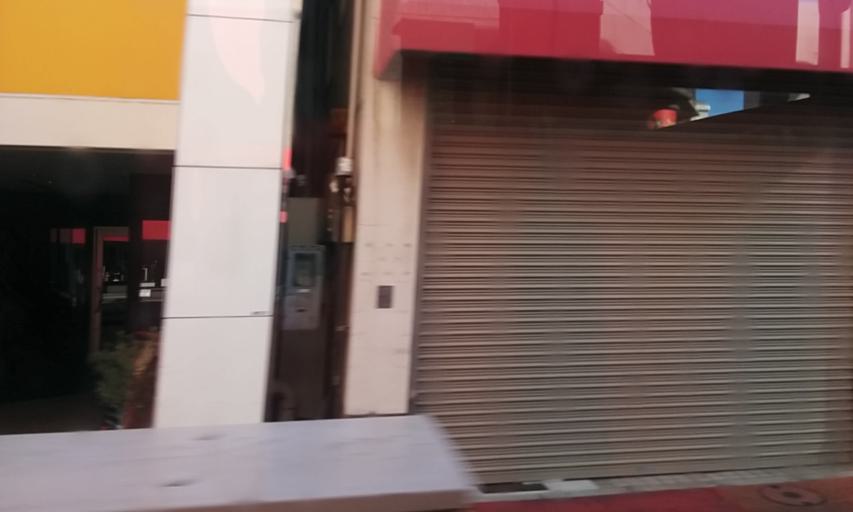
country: JP
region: Wakayama
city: Wakayama-shi
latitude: 34.2341
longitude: 135.1746
